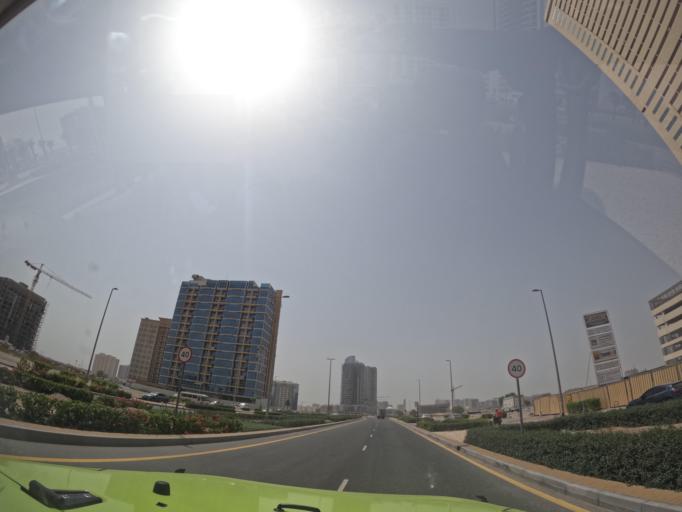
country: AE
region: Dubai
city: Dubai
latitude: 25.0944
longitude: 55.3823
